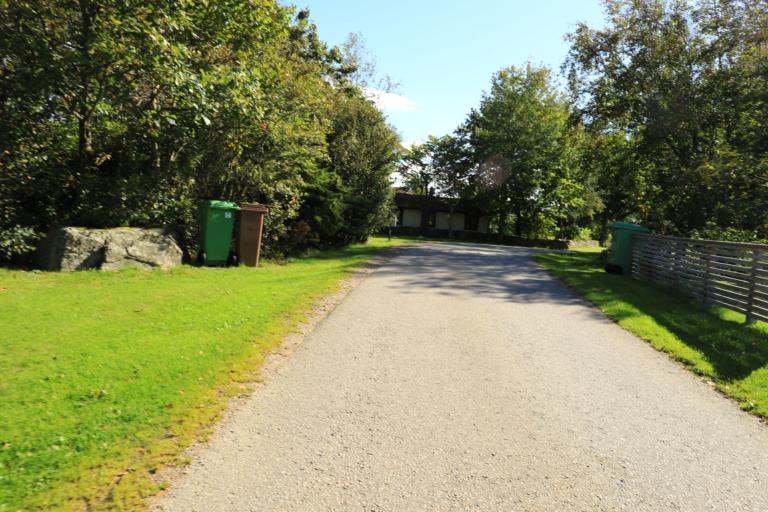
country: SE
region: Halland
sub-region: Varbergs Kommun
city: Traslovslage
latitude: 57.0741
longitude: 12.2659
